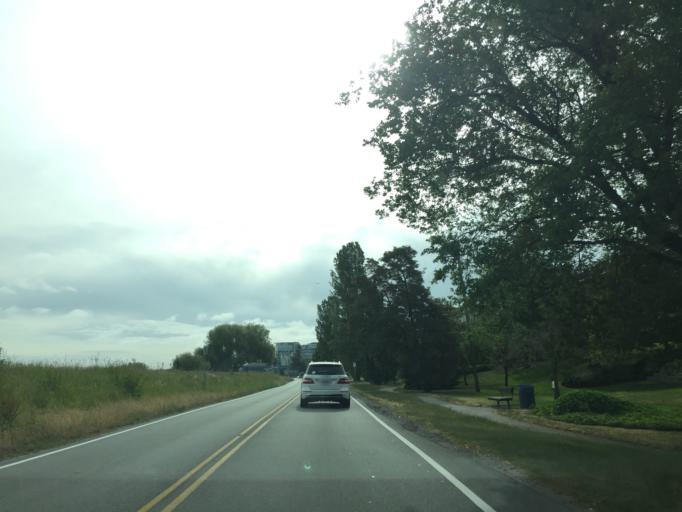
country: CA
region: British Columbia
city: Richmond
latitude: 49.1735
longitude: -123.1645
